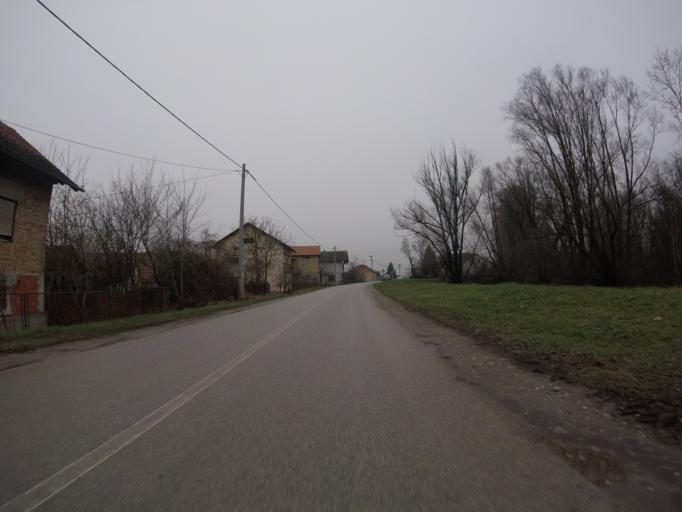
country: HR
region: Sisacko-Moslavacka
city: Lekenik
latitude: 45.6178
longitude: 16.3295
